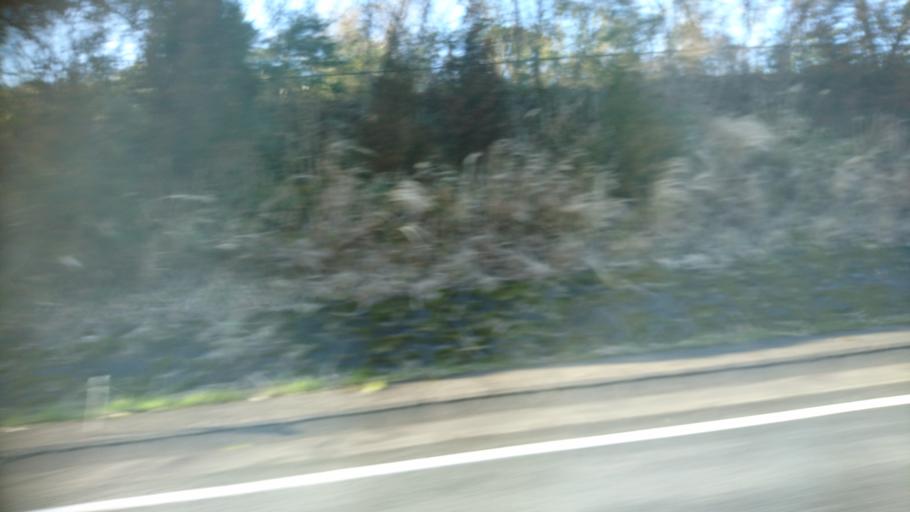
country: JP
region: Miyazaki
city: Kobayashi
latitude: 32.0330
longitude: 130.8083
